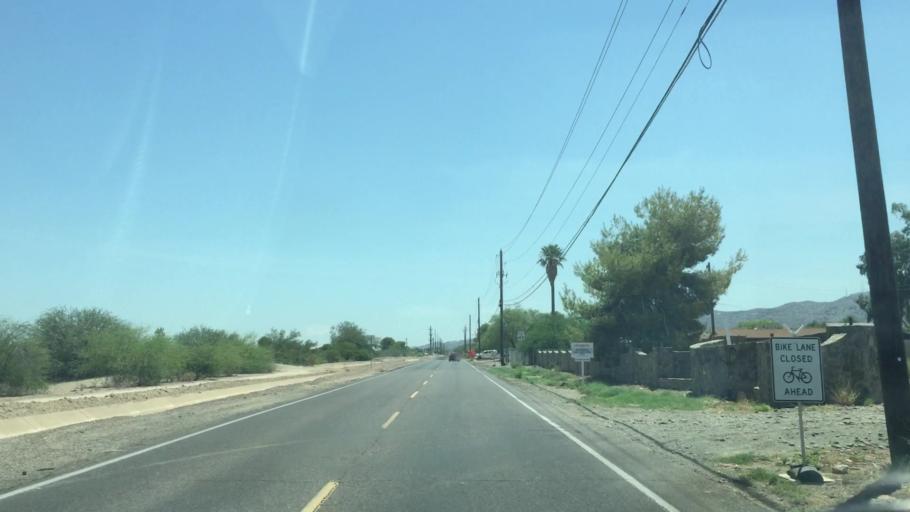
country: US
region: Arizona
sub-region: Maricopa County
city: Laveen
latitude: 33.3630
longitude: -112.1413
